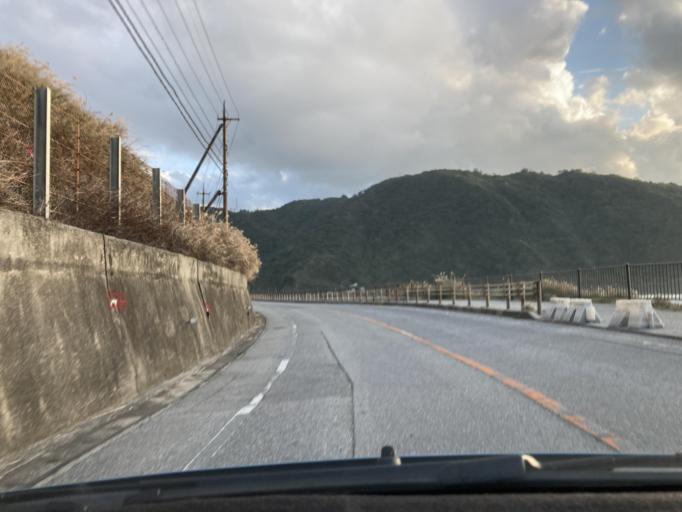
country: JP
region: Okinawa
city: Nago
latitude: 26.8024
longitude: 128.2311
